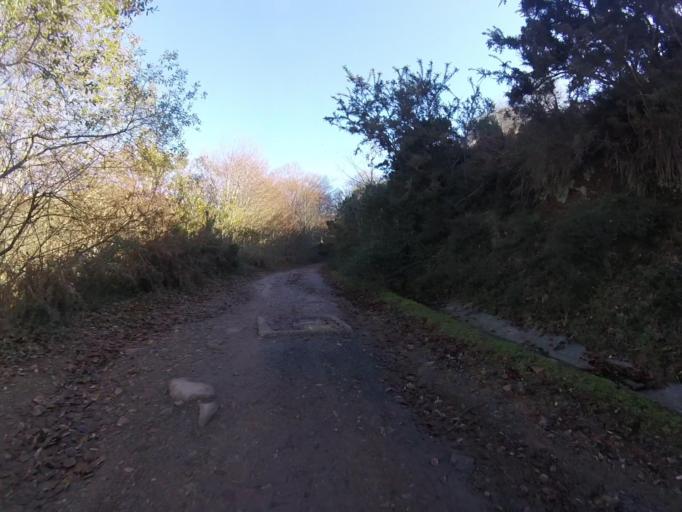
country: ES
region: Navarre
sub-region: Provincia de Navarra
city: Bera
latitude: 43.3009
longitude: -1.6637
